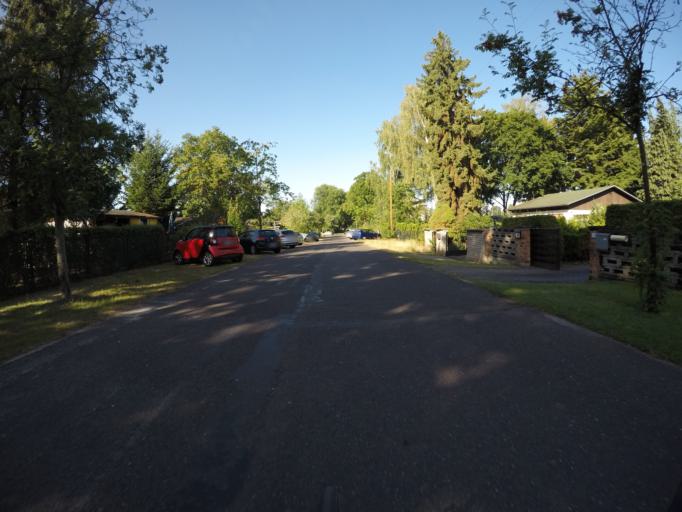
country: DE
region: Berlin
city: Schmockwitz
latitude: 52.3475
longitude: 13.6399
